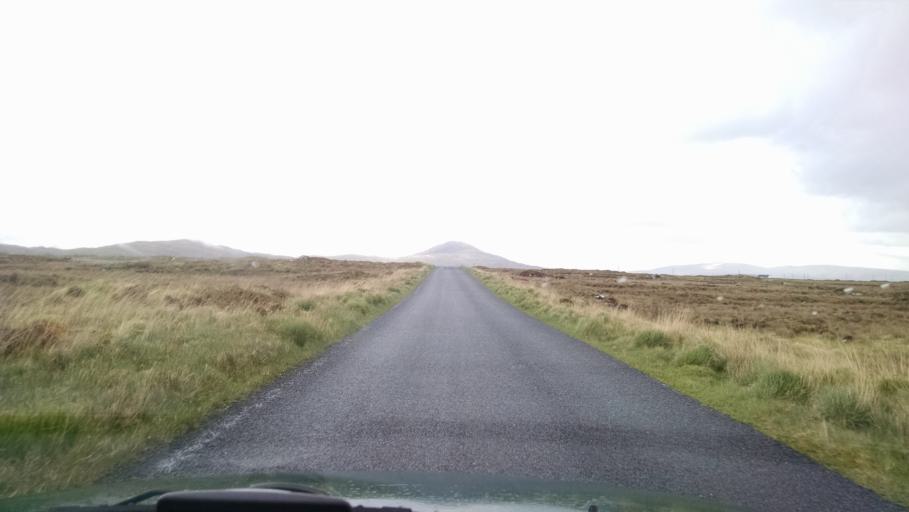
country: IE
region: Connaught
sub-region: County Galway
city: Clifden
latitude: 53.4345
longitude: -9.9006
